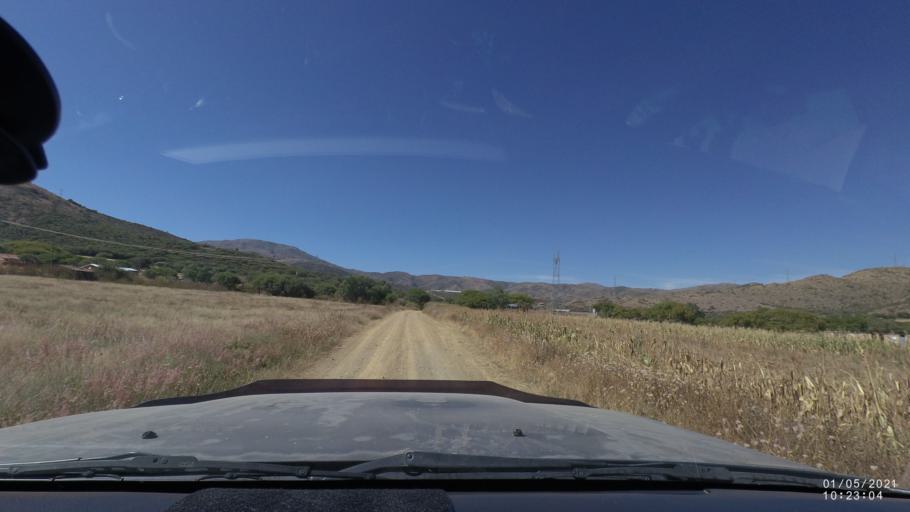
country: BO
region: Cochabamba
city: Capinota
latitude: -17.5704
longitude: -66.1975
